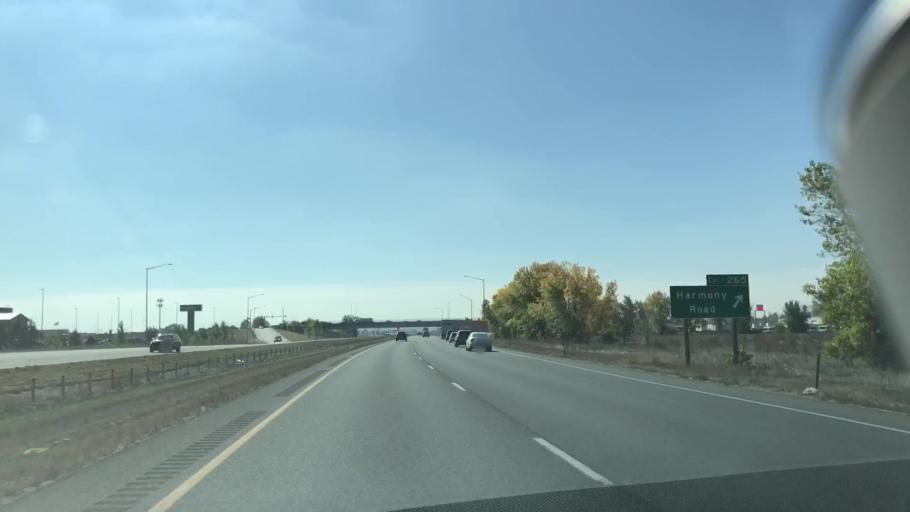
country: US
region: Colorado
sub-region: Weld County
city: Windsor
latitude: 40.5279
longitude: -104.9928
